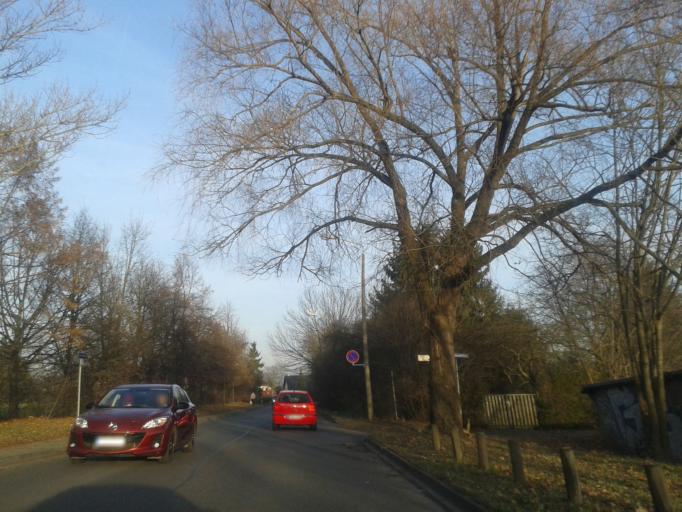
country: DE
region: Saxony
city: Heidenau
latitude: 50.9970
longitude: 13.8076
